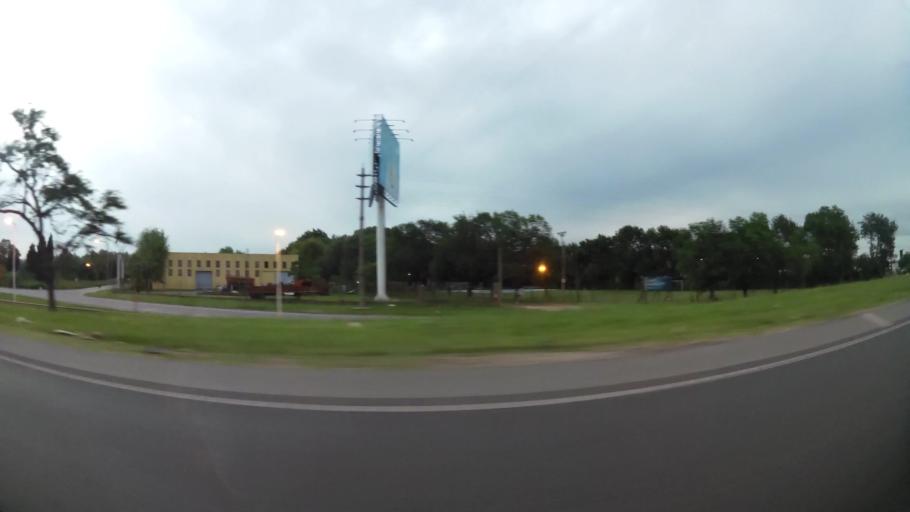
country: AR
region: Santa Fe
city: Granadero Baigorria
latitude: -32.8786
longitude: -60.7077
